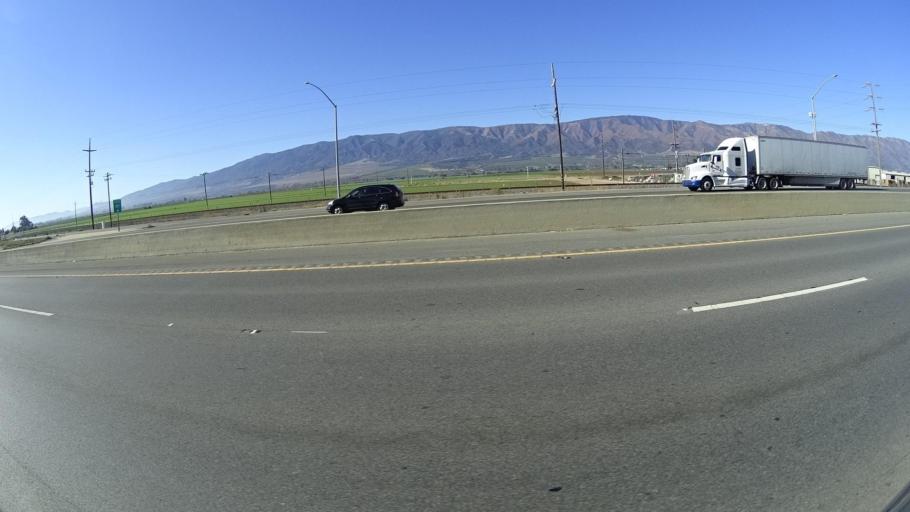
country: US
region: California
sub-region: Monterey County
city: Gonzales
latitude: 36.4680
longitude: -121.3902
